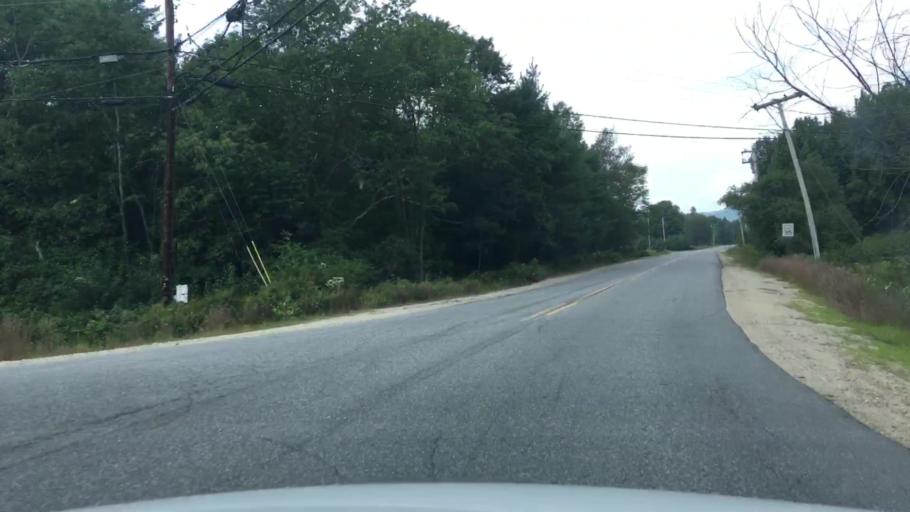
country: US
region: Maine
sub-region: Oxford County
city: Rumford
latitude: 44.5131
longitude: -70.6194
